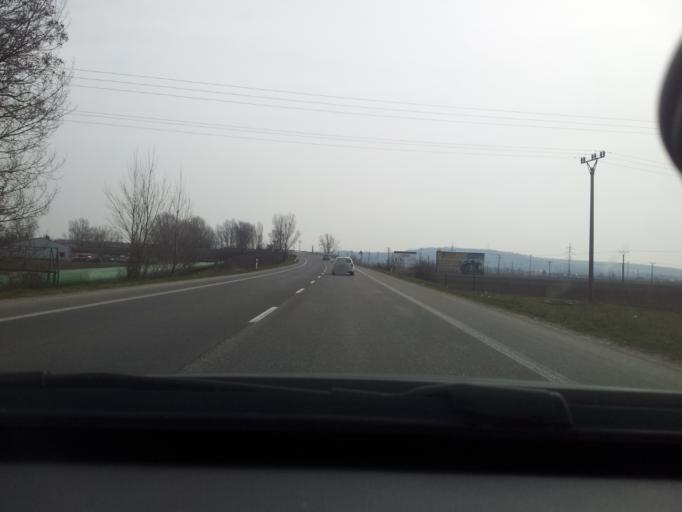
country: SK
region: Trnavsky
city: Leopoldov
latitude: 48.4361
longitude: 17.7518
